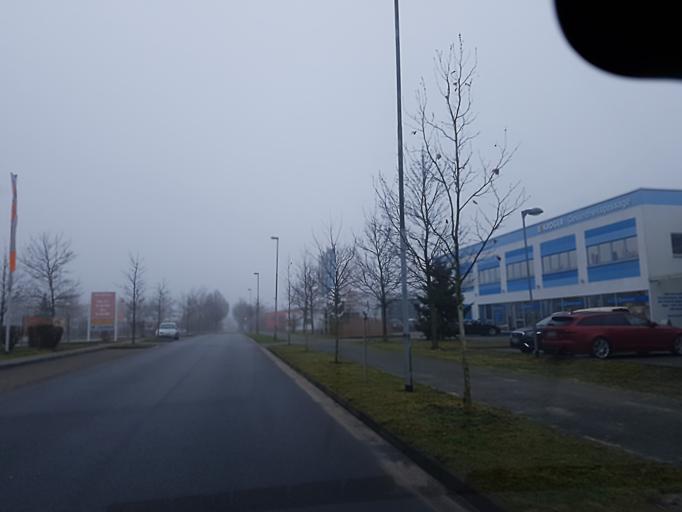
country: DE
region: Brandenburg
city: Finsterwalde
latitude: 51.6350
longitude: 13.7373
